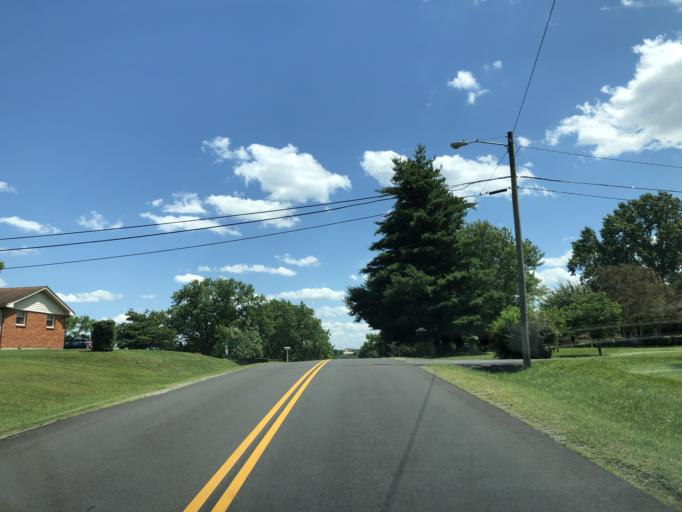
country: US
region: Tennessee
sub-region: Davidson County
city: Nashville
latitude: 36.1718
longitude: -86.7264
